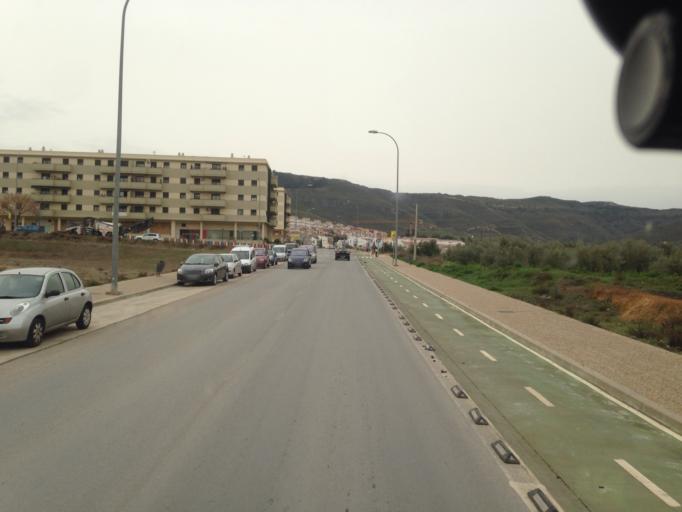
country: ES
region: Andalusia
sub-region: Provincia de Malaga
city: Antequera
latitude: 37.0254
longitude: -4.5742
